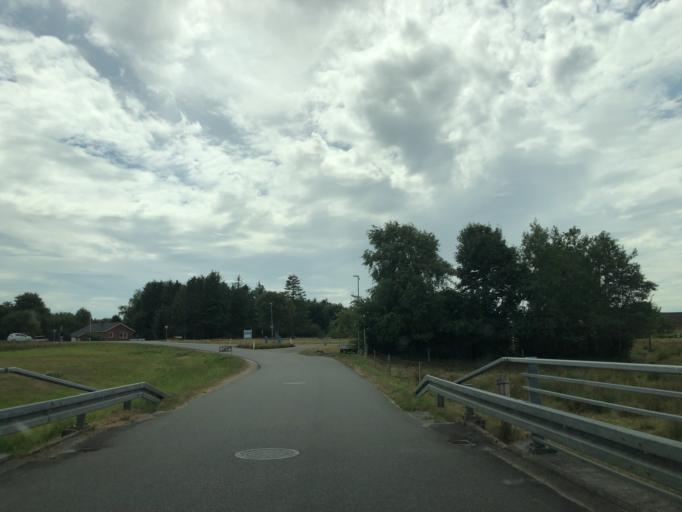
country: DK
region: South Denmark
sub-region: Billund Kommune
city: Grindsted
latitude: 55.6474
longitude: 8.8085
